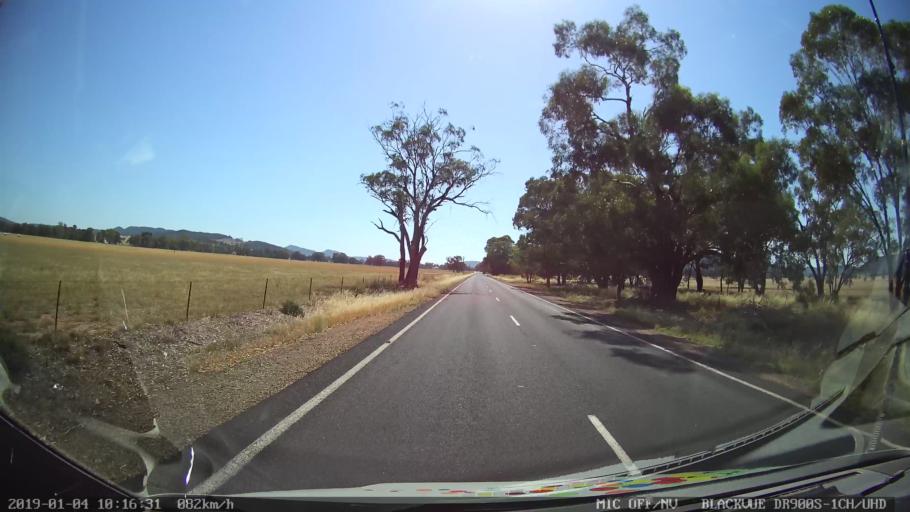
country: AU
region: New South Wales
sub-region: Cabonne
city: Canowindra
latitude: -33.3853
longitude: 148.4378
